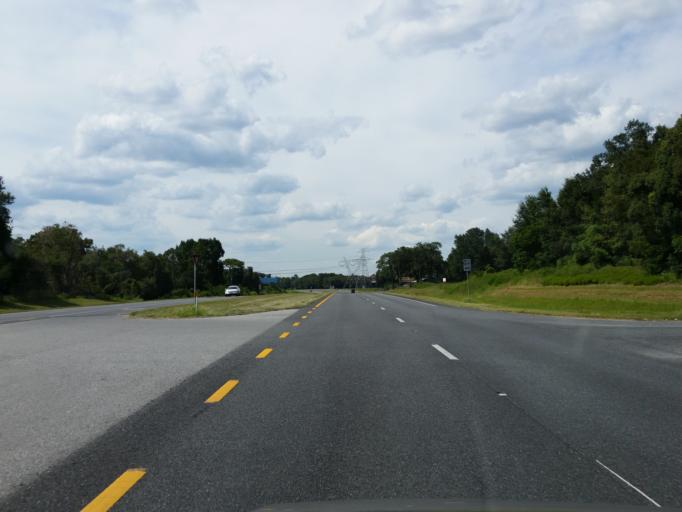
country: US
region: Florida
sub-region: Sumter County
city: Wildwood
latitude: 28.8656
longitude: -82.0787
